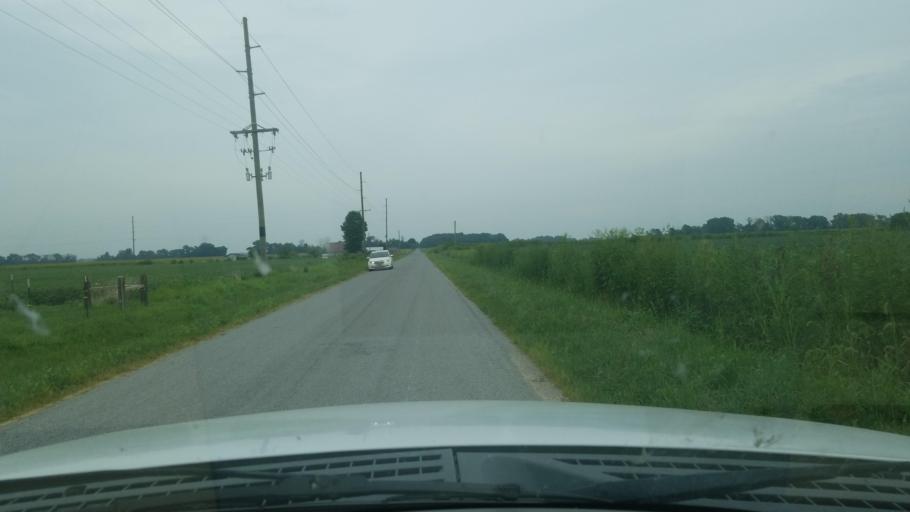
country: US
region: Illinois
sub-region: Saline County
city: Eldorado
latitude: 37.8630
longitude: -88.5062
